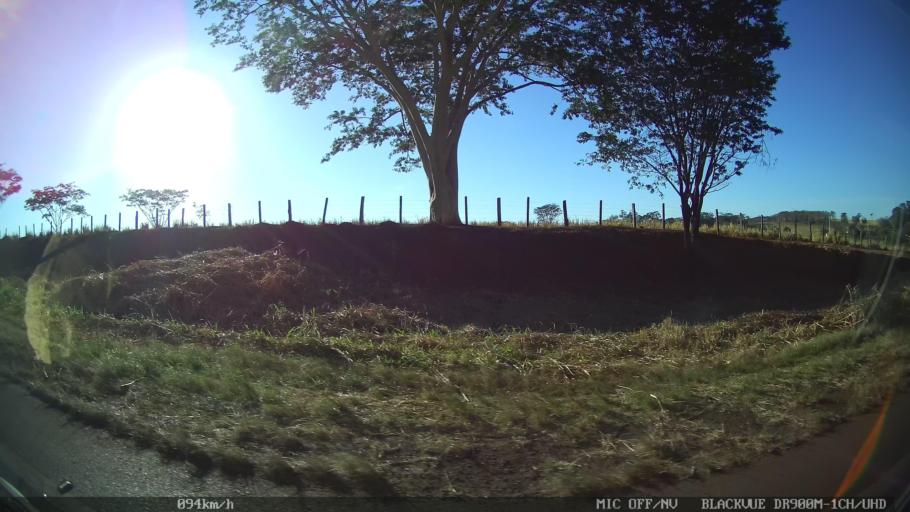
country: BR
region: Sao Paulo
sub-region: Guapiacu
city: Guapiacu
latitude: -20.7671
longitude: -49.2020
